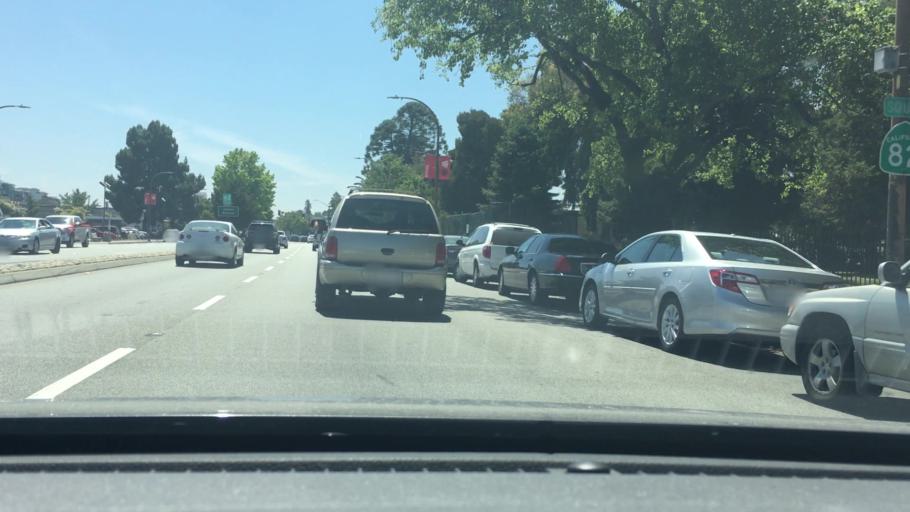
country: US
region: California
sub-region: San Mateo County
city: Redwood City
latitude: 37.4859
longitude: -122.2347
